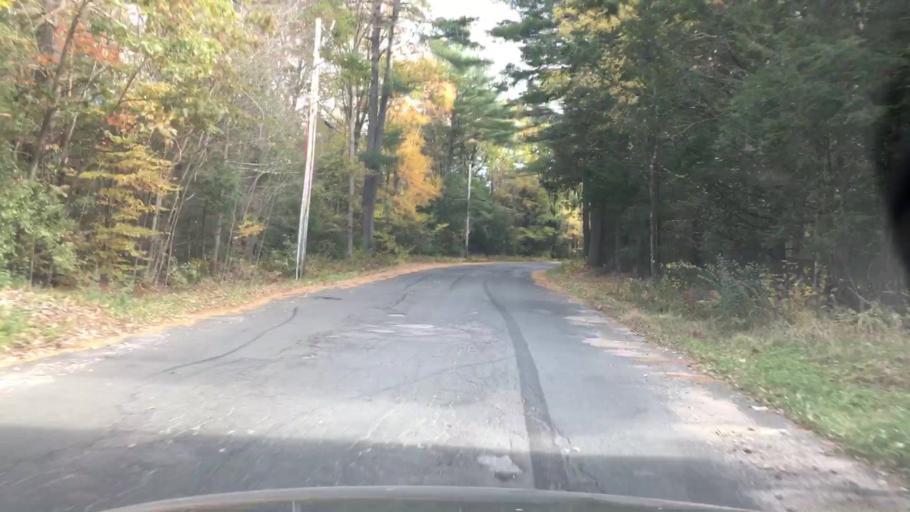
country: US
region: Connecticut
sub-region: Tolland County
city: Stafford
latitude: 41.9950
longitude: -72.3298
